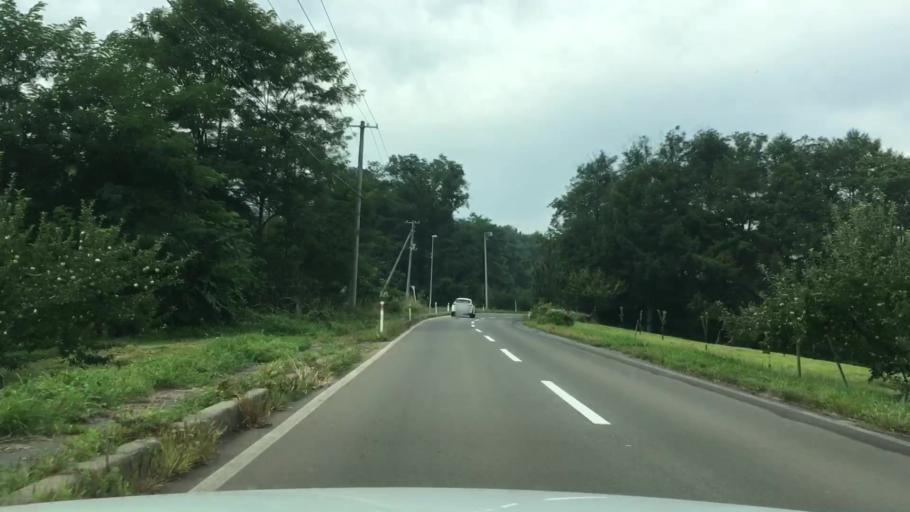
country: JP
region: Aomori
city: Hirosaki
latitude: 40.6687
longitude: 140.3910
